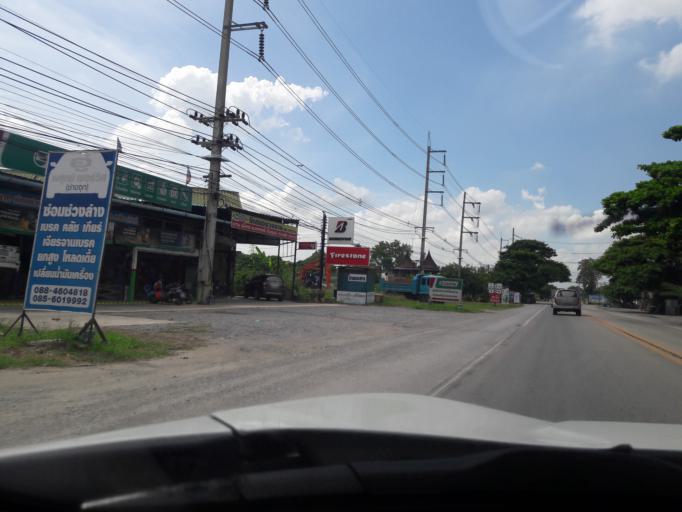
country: TH
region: Ang Thong
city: Ban Thai Tan
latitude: 14.5797
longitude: 100.5014
